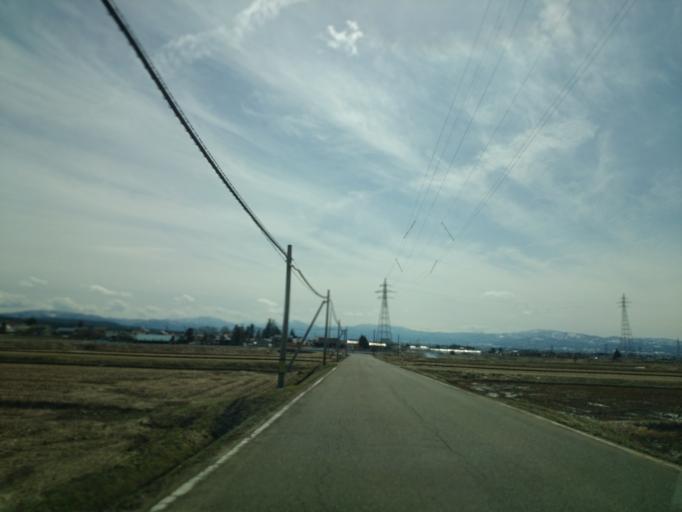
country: JP
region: Fukushima
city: Kitakata
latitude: 37.6480
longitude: 139.9105
